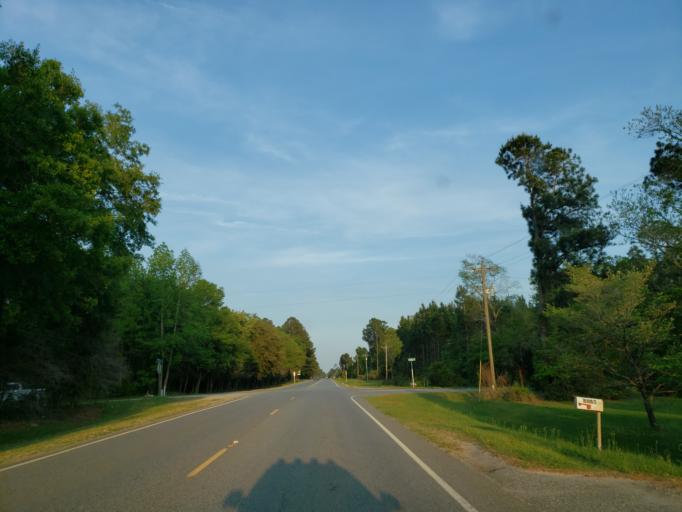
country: US
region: Georgia
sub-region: Lowndes County
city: Hahira
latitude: 30.9956
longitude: -83.4308
